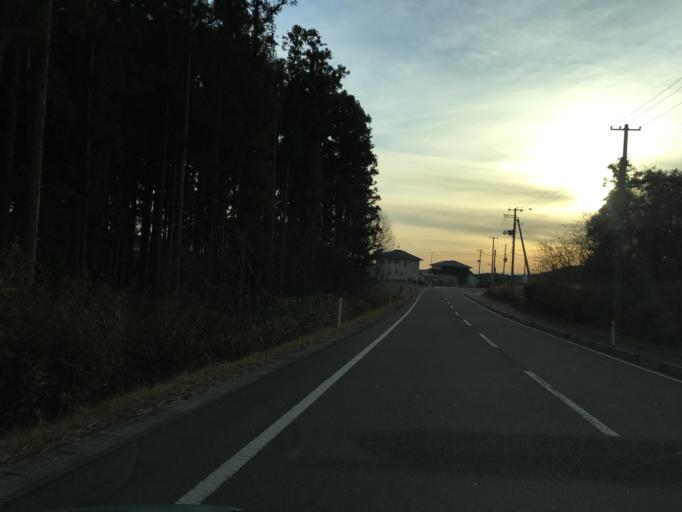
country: JP
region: Miyagi
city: Kogota
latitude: 38.6961
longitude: 141.1008
